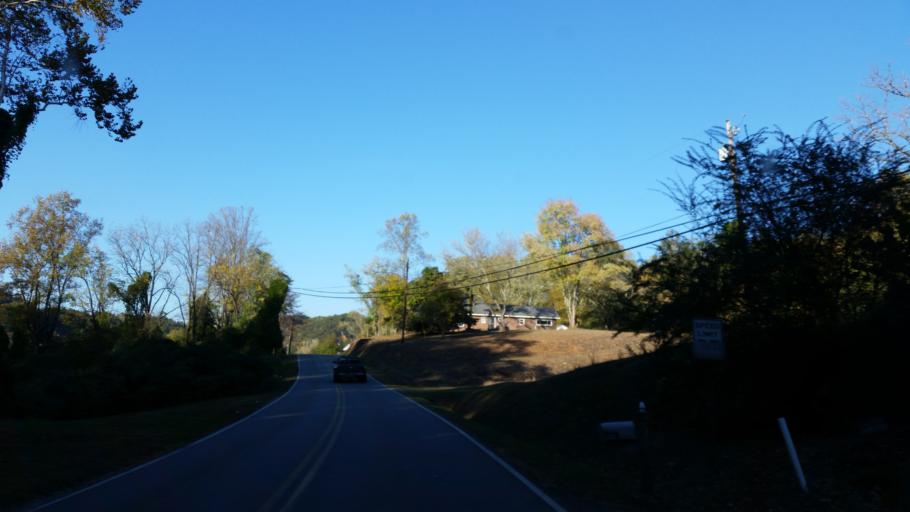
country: US
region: Georgia
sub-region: Gilmer County
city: Ellijay
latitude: 34.6797
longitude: -84.4746
